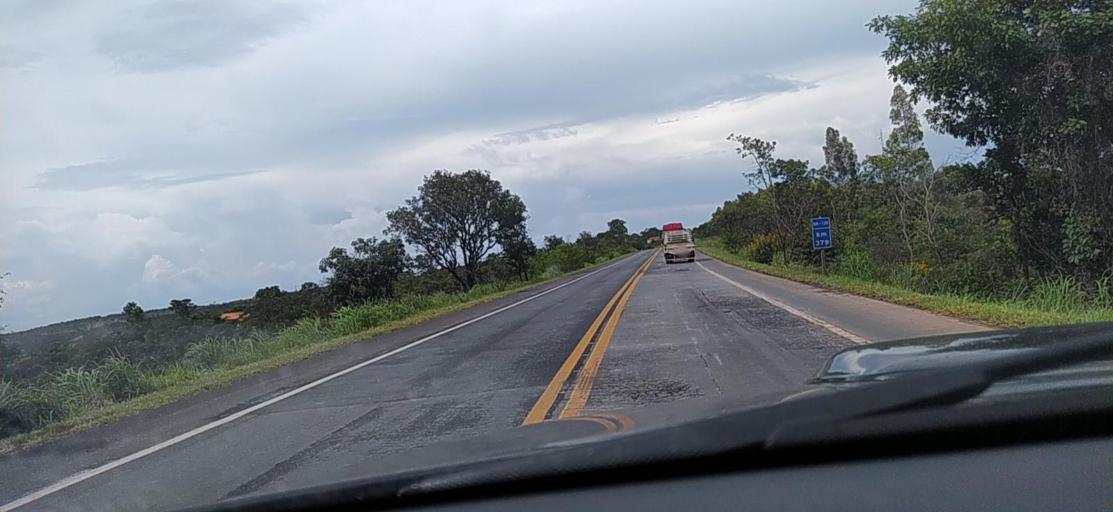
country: BR
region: Minas Gerais
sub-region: Montes Claros
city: Montes Claros
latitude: -16.8460
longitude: -43.8513
